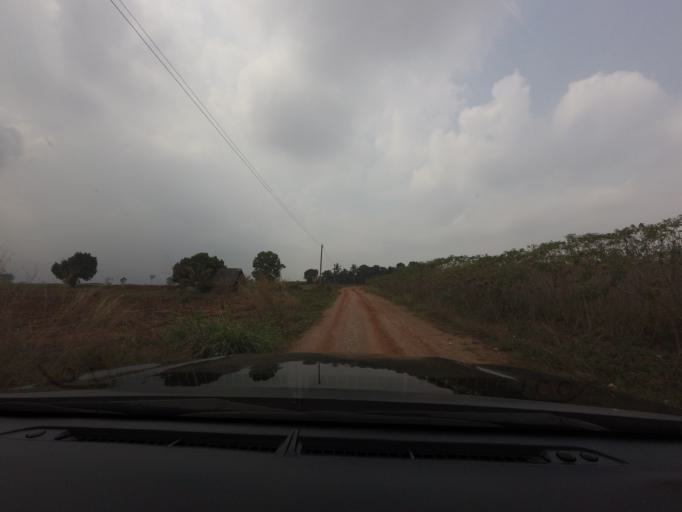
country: TH
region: Nakhon Ratchasima
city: Wang Nam Khiao
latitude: 14.4781
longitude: 101.6430
